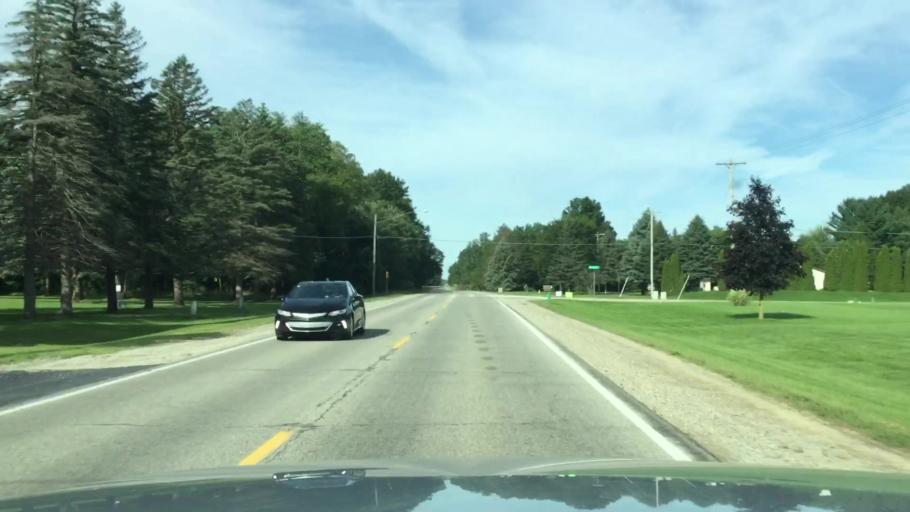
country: US
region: Michigan
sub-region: Genesee County
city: Flushing
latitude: 43.1179
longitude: -83.8326
